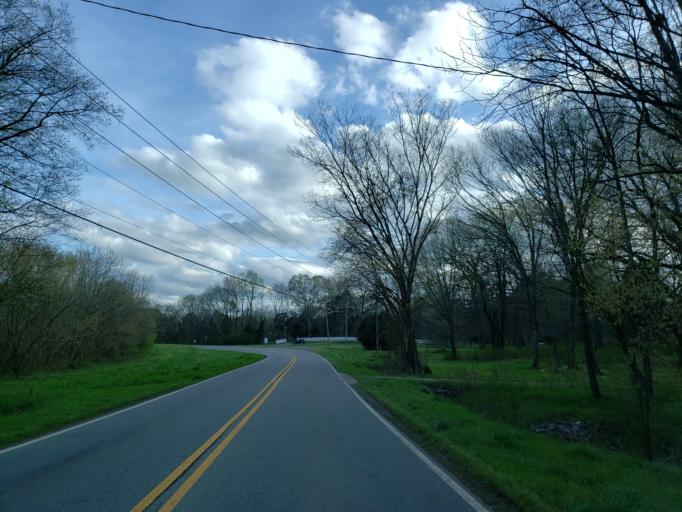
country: US
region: Georgia
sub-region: Bartow County
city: Cartersville
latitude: 34.2237
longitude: -84.8047
